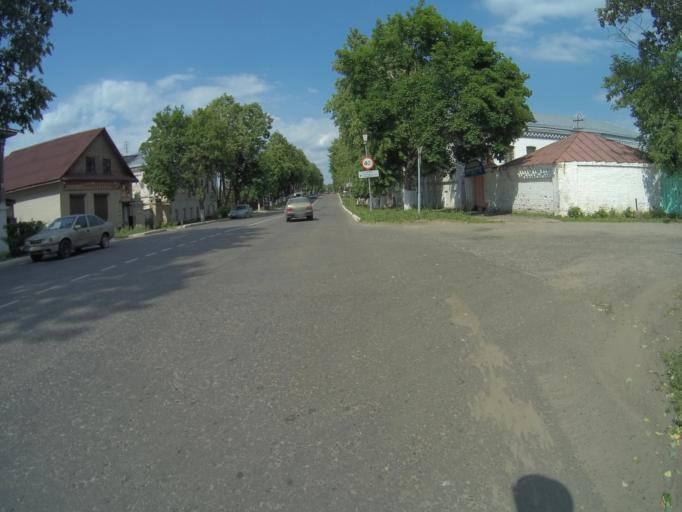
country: RU
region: Vladimir
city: Suzdal'
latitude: 56.4099
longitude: 40.4468
